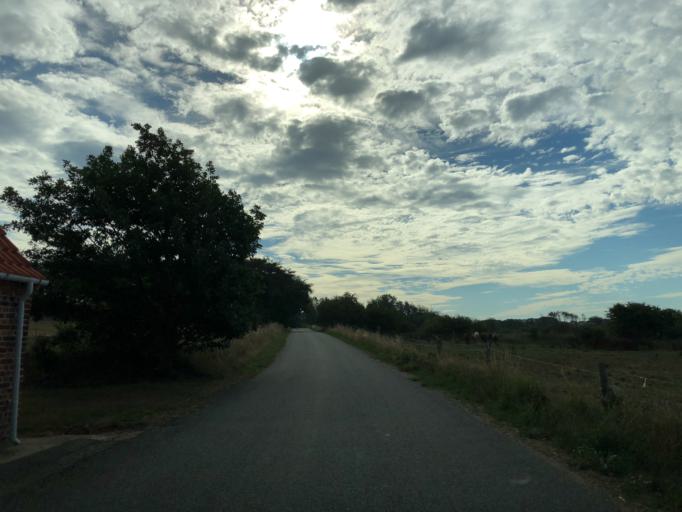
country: DK
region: Central Jutland
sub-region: Ringkobing-Skjern Kommune
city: Skjern
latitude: 56.0443
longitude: 8.4216
